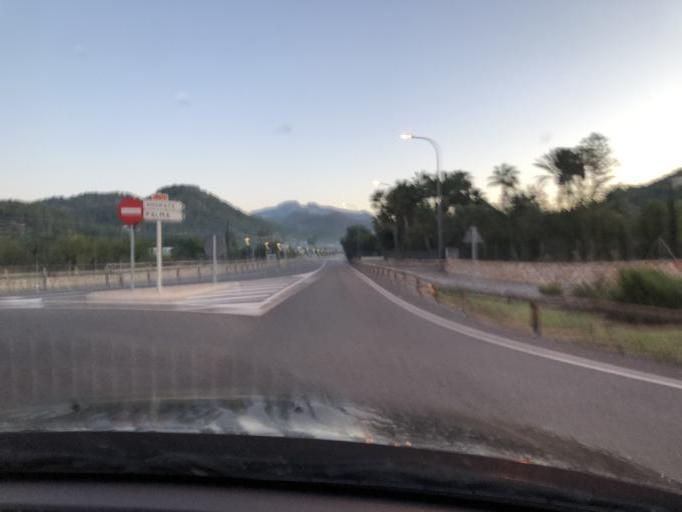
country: ES
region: Balearic Islands
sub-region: Illes Balears
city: Andratx
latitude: 39.5601
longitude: 2.4006
